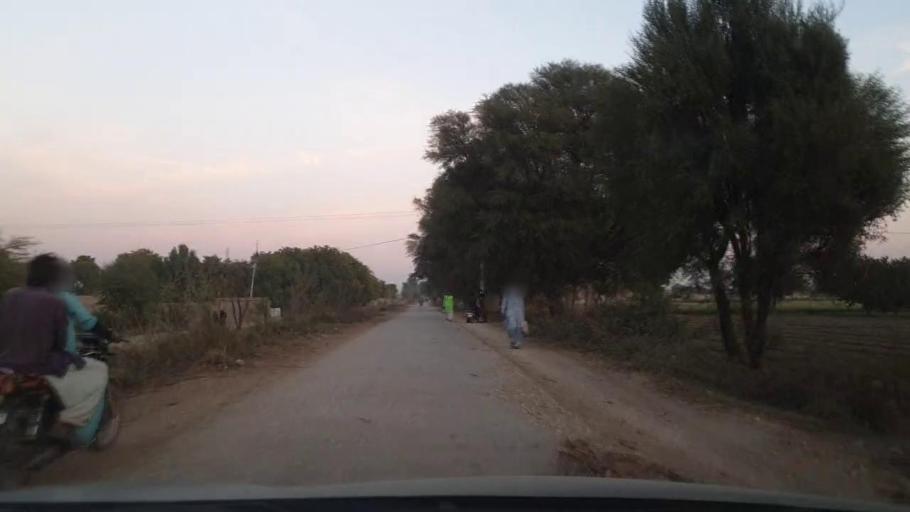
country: PK
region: Sindh
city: Tando Allahyar
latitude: 25.5535
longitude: 68.7936
